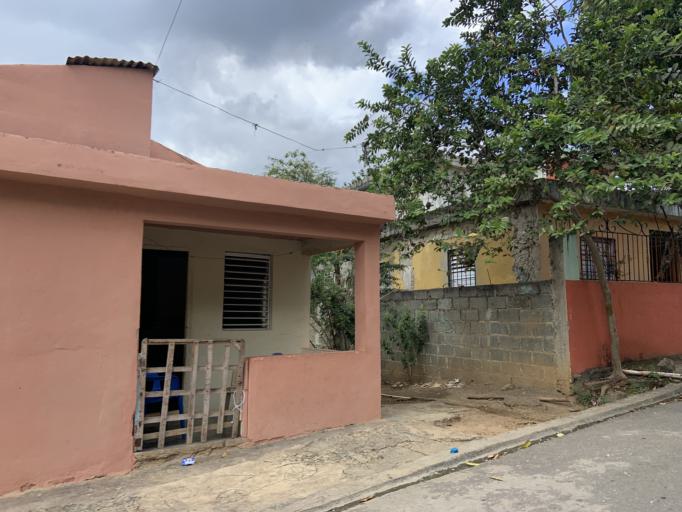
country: DO
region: Monte Plata
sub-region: Yamasa
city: Yamasa
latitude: 18.7719
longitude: -70.0218
